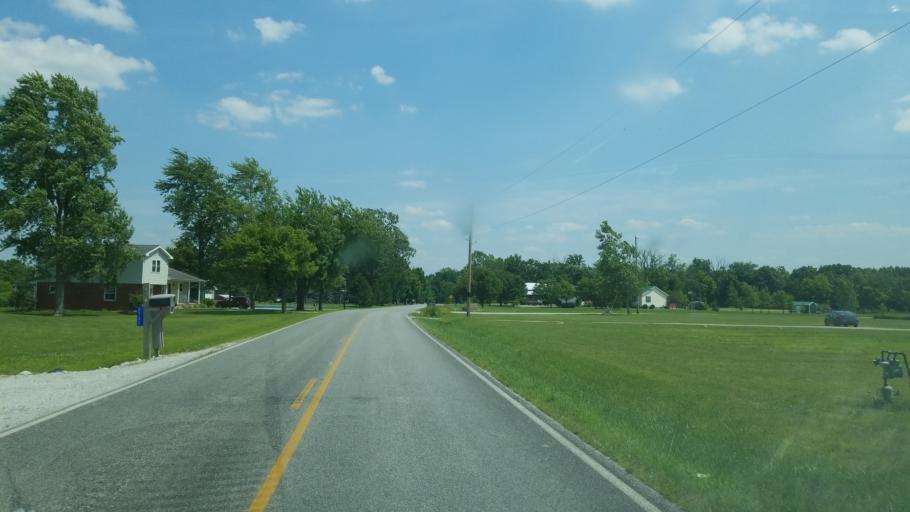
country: US
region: Ohio
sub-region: Seneca County
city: Tiffin
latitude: 41.1628
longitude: -83.2094
